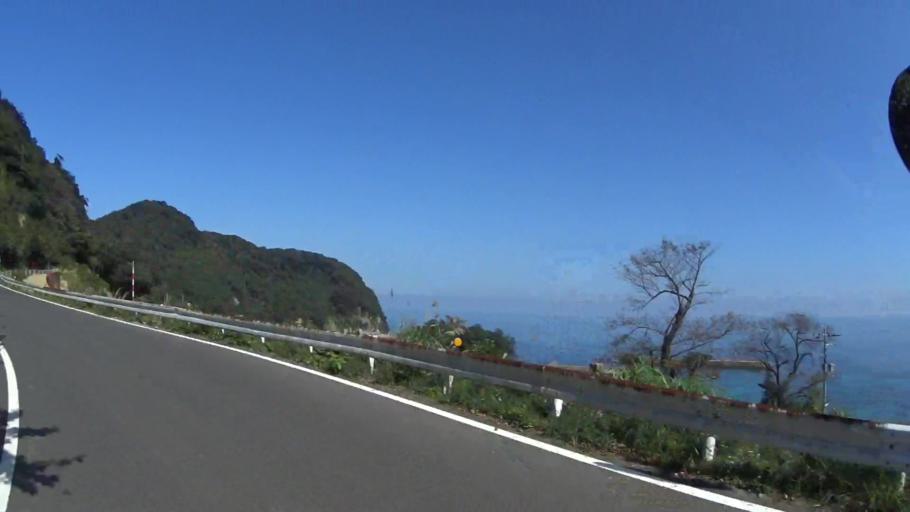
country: JP
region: Kyoto
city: Miyazu
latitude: 35.7516
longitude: 135.2497
